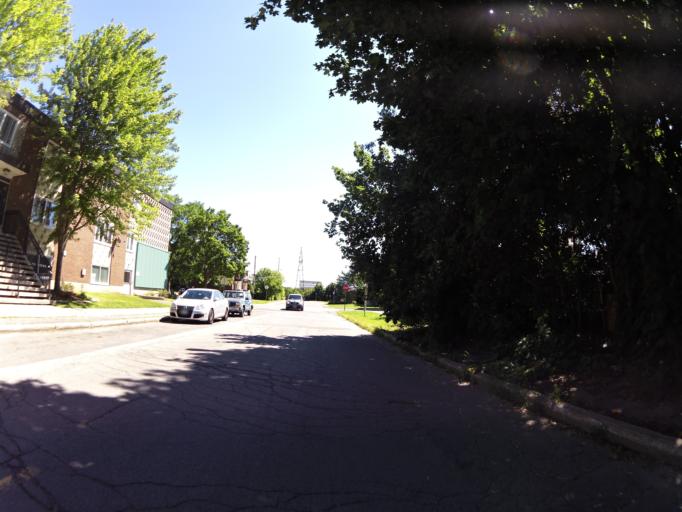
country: CA
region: Ontario
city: Ottawa
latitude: 45.4256
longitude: -75.6423
